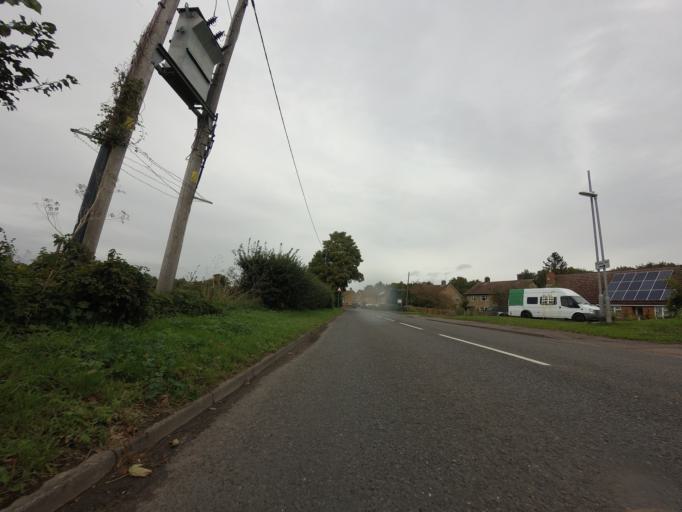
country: GB
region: England
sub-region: Cambridgeshire
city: Harston
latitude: 52.0882
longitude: 0.0744
